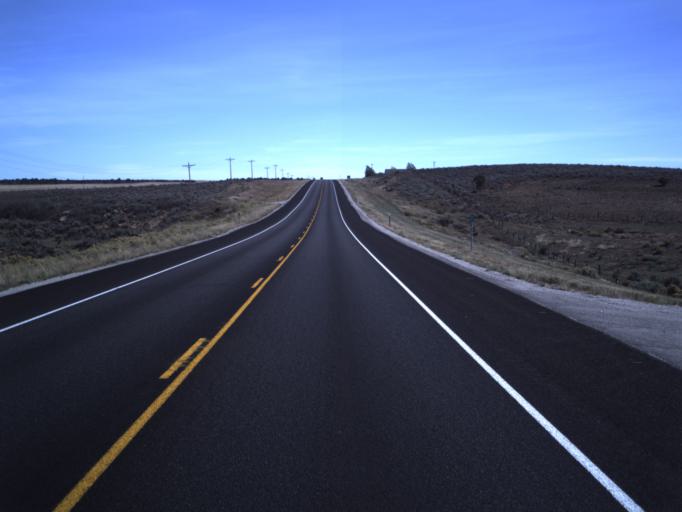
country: US
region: Utah
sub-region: San Juan County
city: Monticello
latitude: 37.8702
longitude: -109.2520
